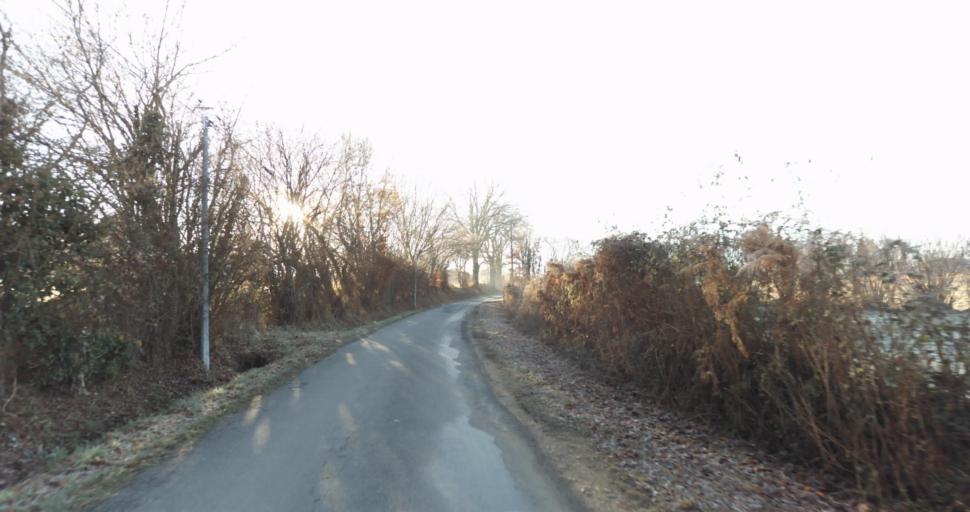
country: FR
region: Limousin
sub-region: Departement de la Haute-Vienne
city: Aixe-sur-Vienne
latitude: 45.8174
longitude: 1.1420
